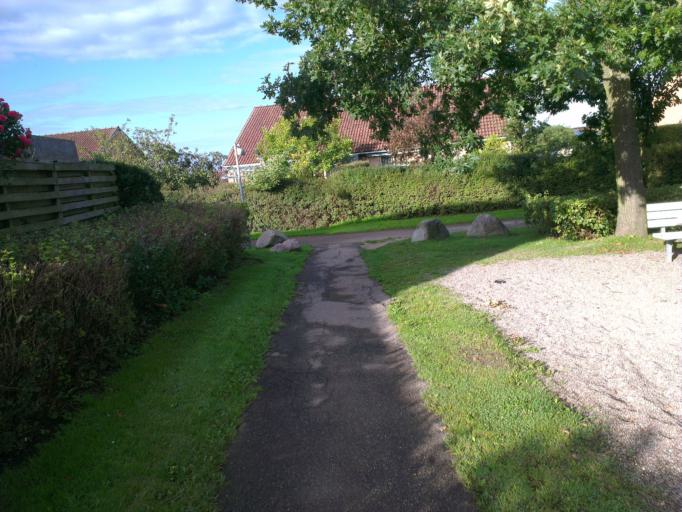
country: DK
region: Capital Region
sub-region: Frederikssund Kommune
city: Frederikssund
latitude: 55.8579
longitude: 12.0744
